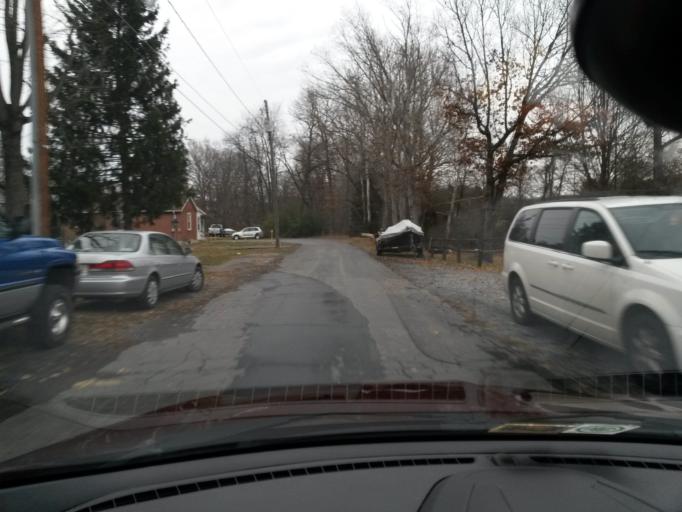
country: US
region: Virginia
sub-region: Alleghany County
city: Clifton Forge
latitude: 37.8221
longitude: -79.7959
